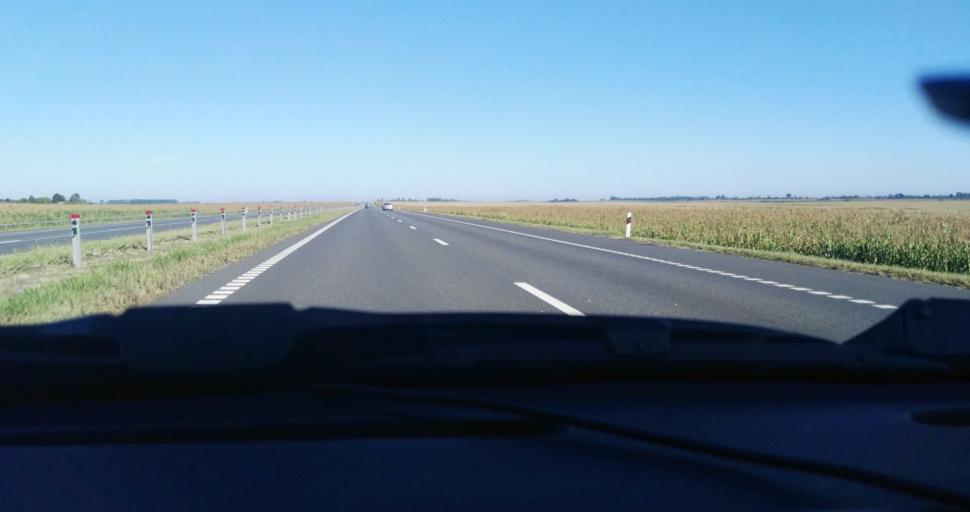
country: BY
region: Gomel
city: Buda-Kashalyova
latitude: 52.5256
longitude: 30.6167
